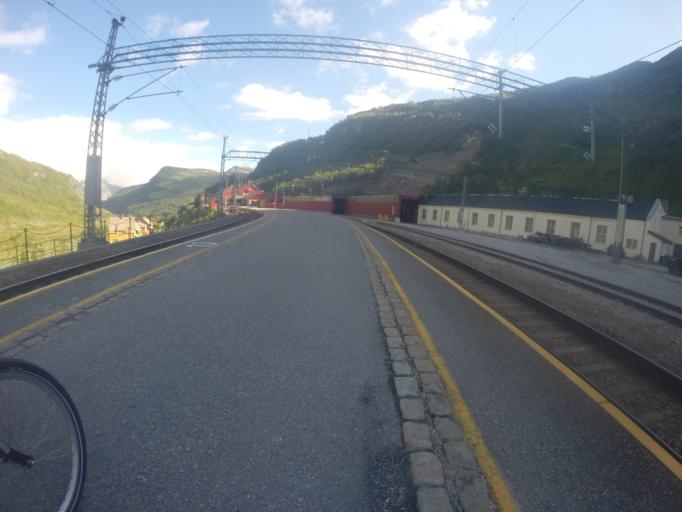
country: NO
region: Sogn og Fjordane
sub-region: Aurland
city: Aurlandsvangen
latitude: 60.7340
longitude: 7.1223
